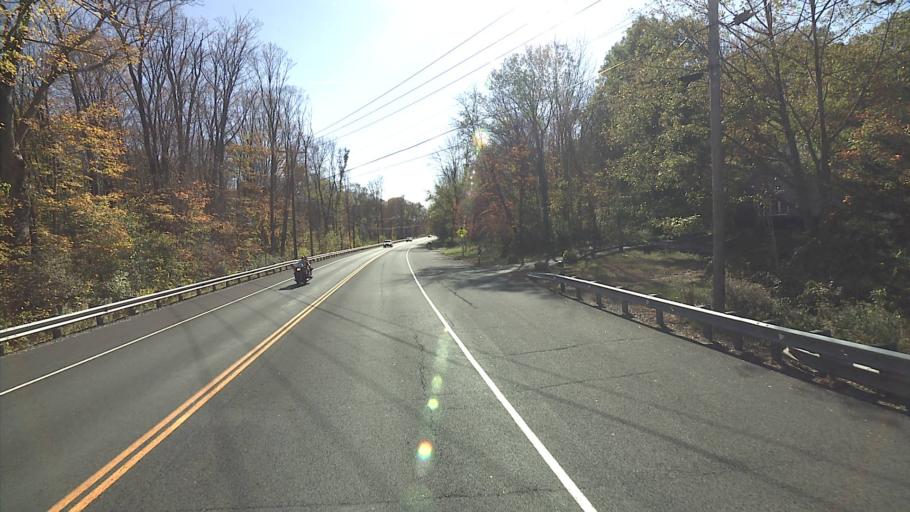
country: US
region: Connecticut
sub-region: Tolland County
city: Coventry Lake
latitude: 41.7783
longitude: -72.4181
